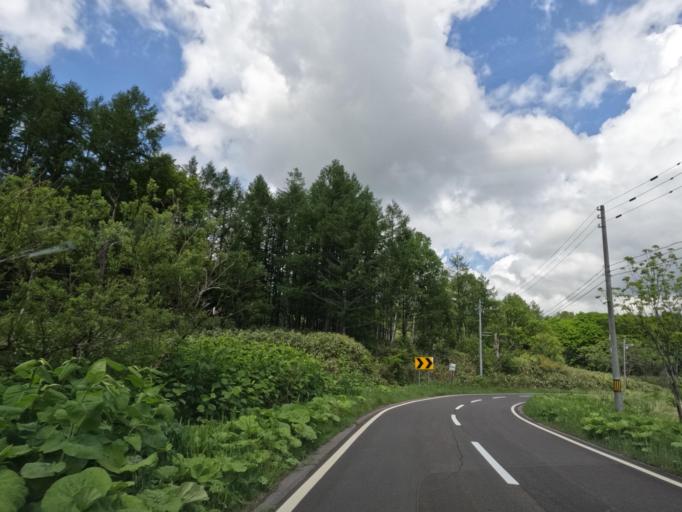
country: JP
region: Hokkaido
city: Takikawa
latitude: 43.5510
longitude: 141.6540
